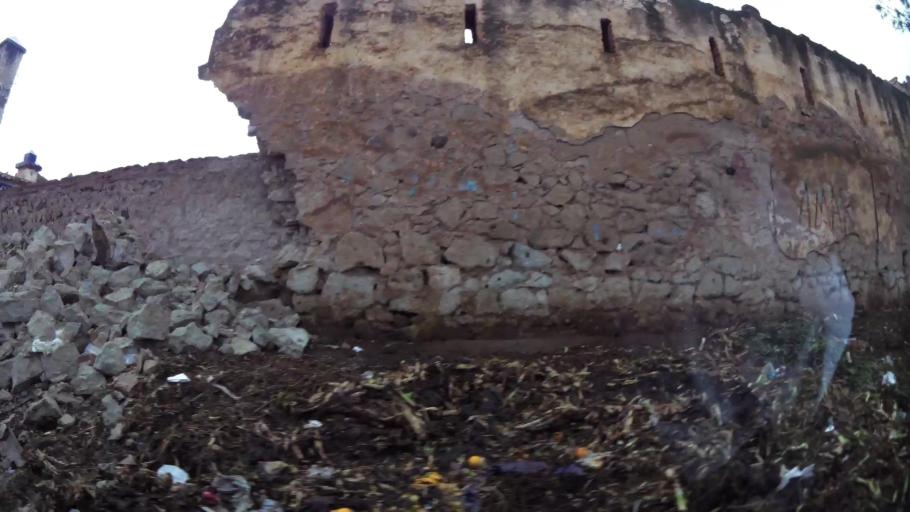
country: MA
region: Oriental
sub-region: Nador
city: Nador
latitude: 35.1512
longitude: -3.0049
